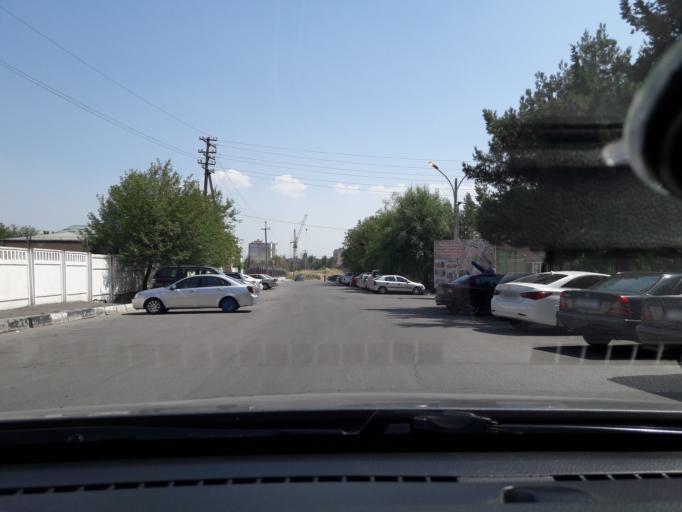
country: TJ
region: Dushanbe
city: Dushanbe
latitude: 38.5767
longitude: 68.7490
